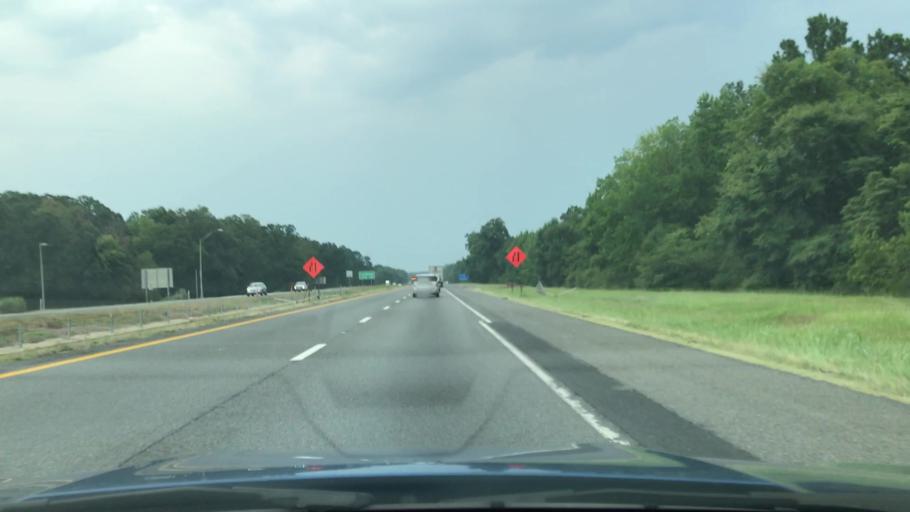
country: US
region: Texas
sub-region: Harrison County
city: Waskom
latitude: 32.4621
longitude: -94.0450
